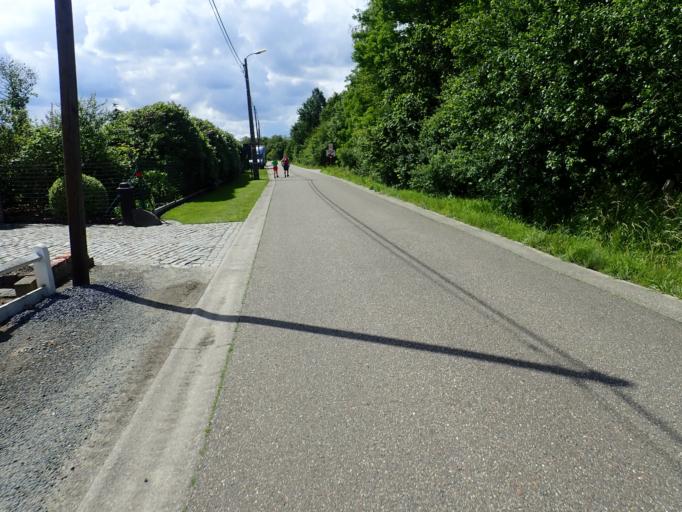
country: BE
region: Flanders
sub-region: Provincie Antwerpen
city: Heist-op-den-Berg
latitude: 51.0896
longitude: 4.7289
